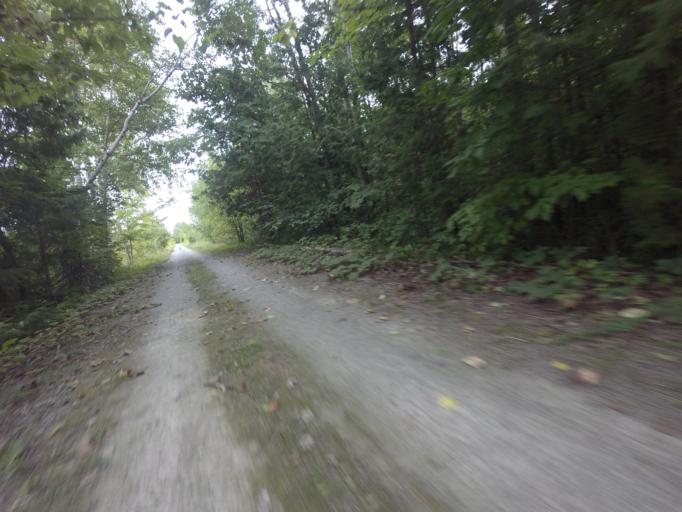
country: CA
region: Ontario
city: Uxbridge
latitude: 44.3003
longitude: -78.9274
